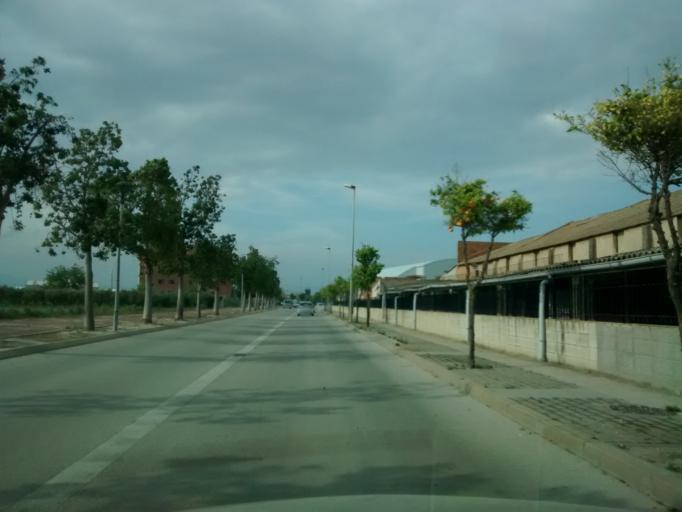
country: ES
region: Catalonia
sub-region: Provincia de Tarragona
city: Deltebre
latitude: 40.7198
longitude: 0.7211
